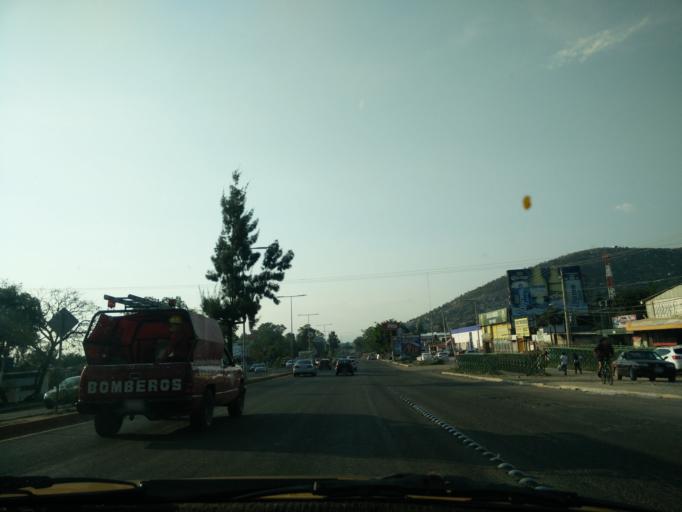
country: MX
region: Oaxaca
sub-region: Santa Maria Atzompa
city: San Jeronimo Yahuiche
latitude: 17.0981
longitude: -96.7502
